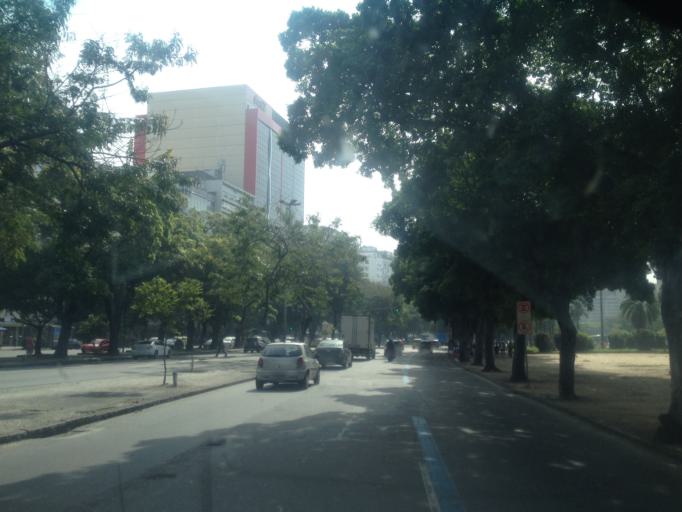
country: BR
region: Rio de Janeiro
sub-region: Rio De Janeiro
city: Rio de Janeiro
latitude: -22.9486
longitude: -43.1819
